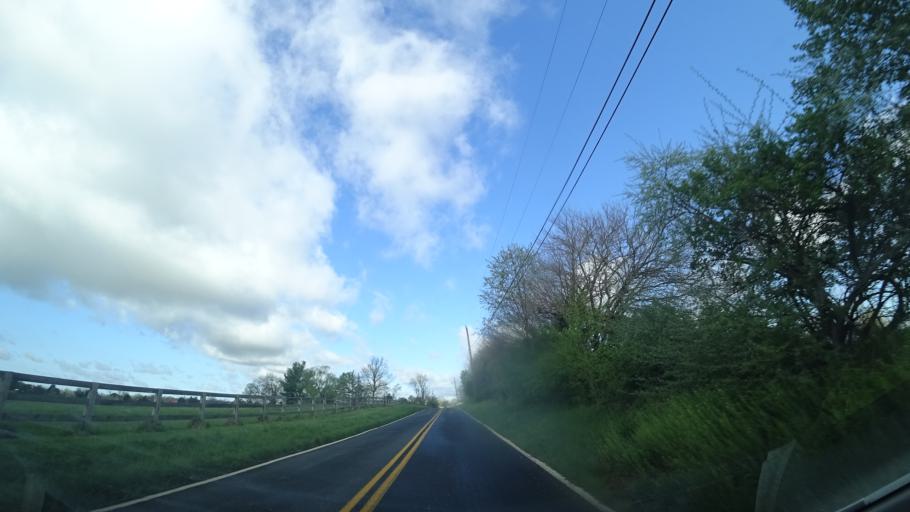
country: US
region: Virginia
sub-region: Loudoun County
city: Lowes Island
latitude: 39.1046
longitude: -77.3750
